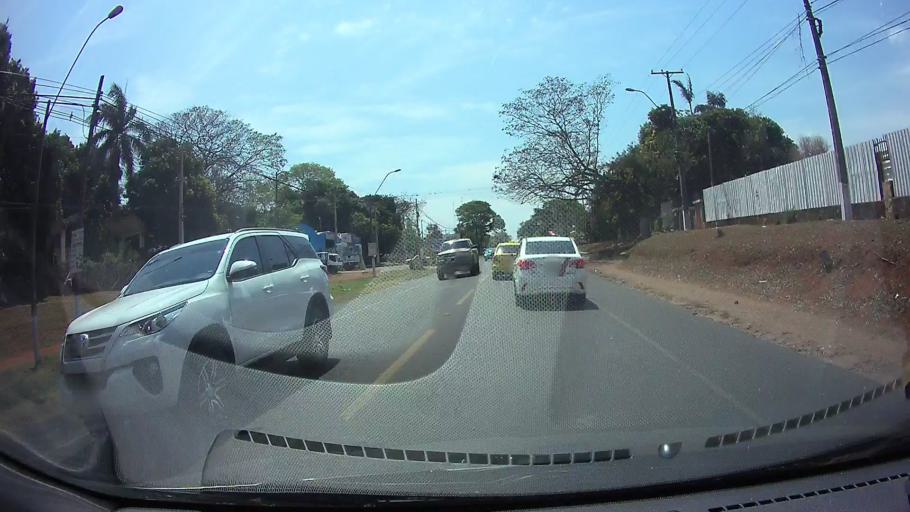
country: PY
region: Central
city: Capiata
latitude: -25.3857
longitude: -57.4720
